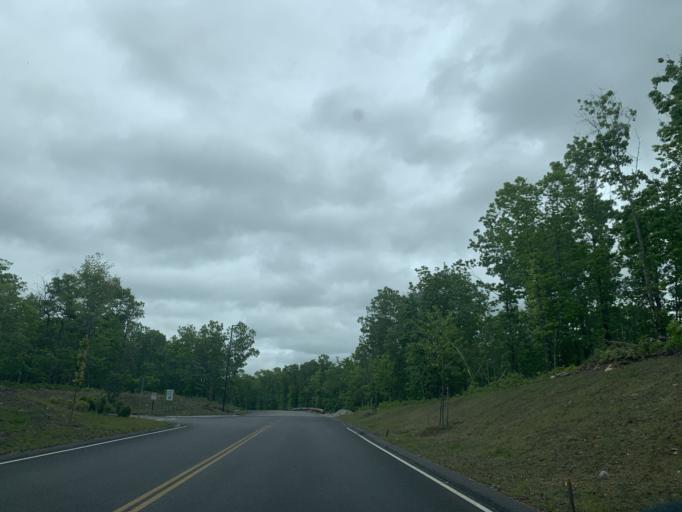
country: US
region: Massachusetts
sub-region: Worcester County
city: Uxbridge
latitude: 42.0623
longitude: -71.6628
